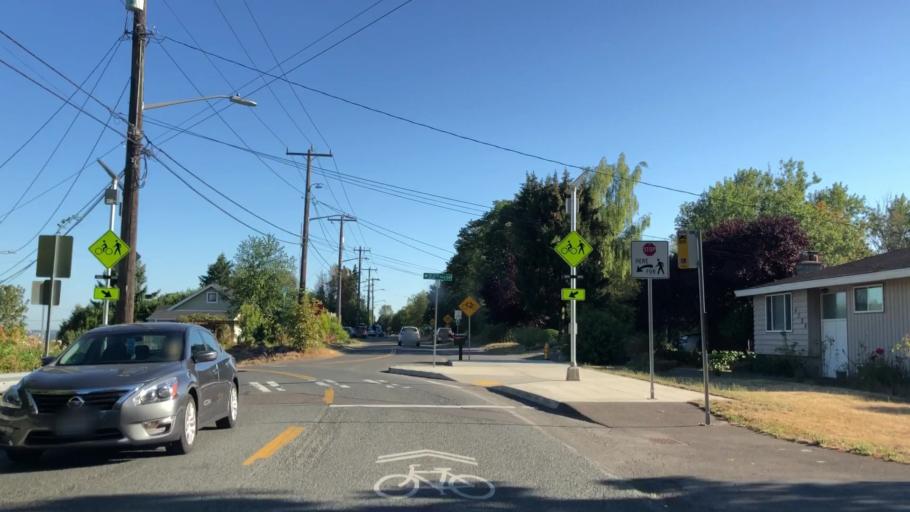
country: US
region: Washington
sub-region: King County
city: White Center
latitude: 47.5593
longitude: -122.3602
